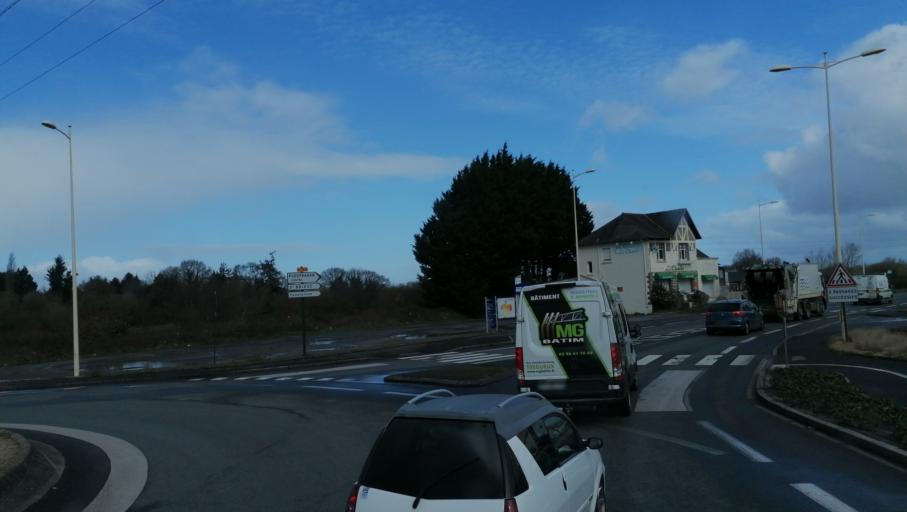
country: FR
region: Brittany
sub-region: Departement des Cotes-d'Armor
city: Ploufragan
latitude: 48.4716
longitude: -2.8018
